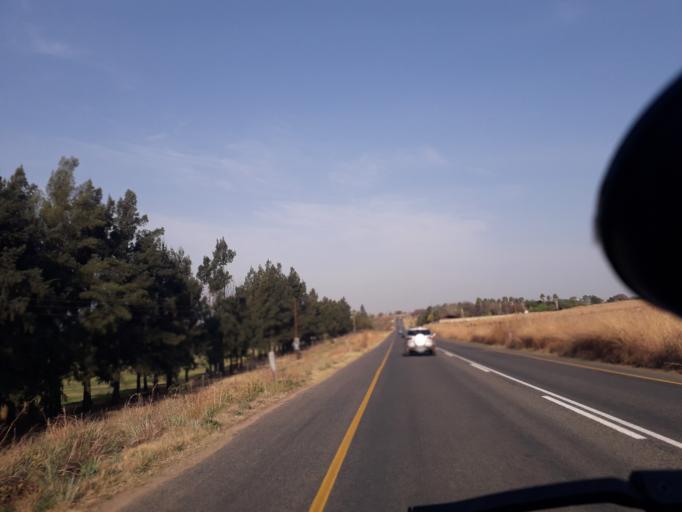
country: ZA
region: Gauteng
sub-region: West Rand District Municipality
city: Muldersdriseloop
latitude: -25.9608
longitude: 27.8892
